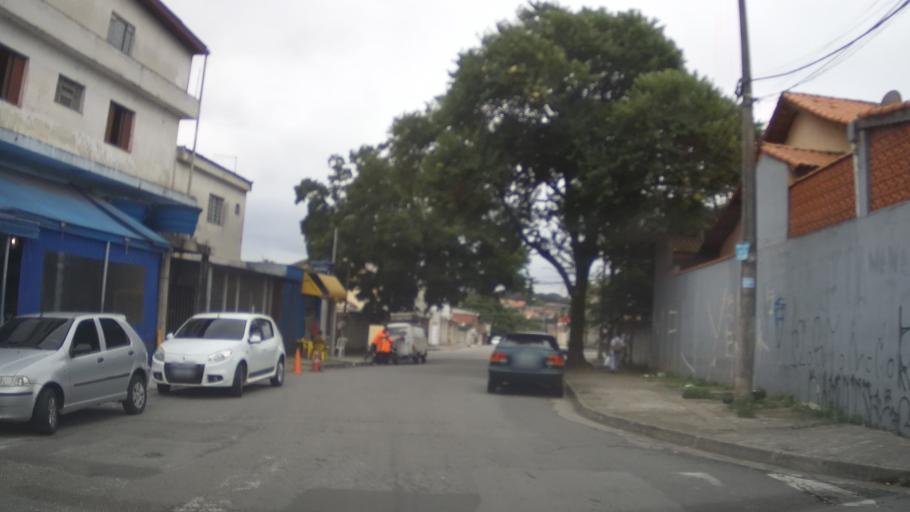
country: BR
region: Sao Paulo
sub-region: Guarulhos
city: Guarulhos
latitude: -23.4470
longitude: -46.5107
